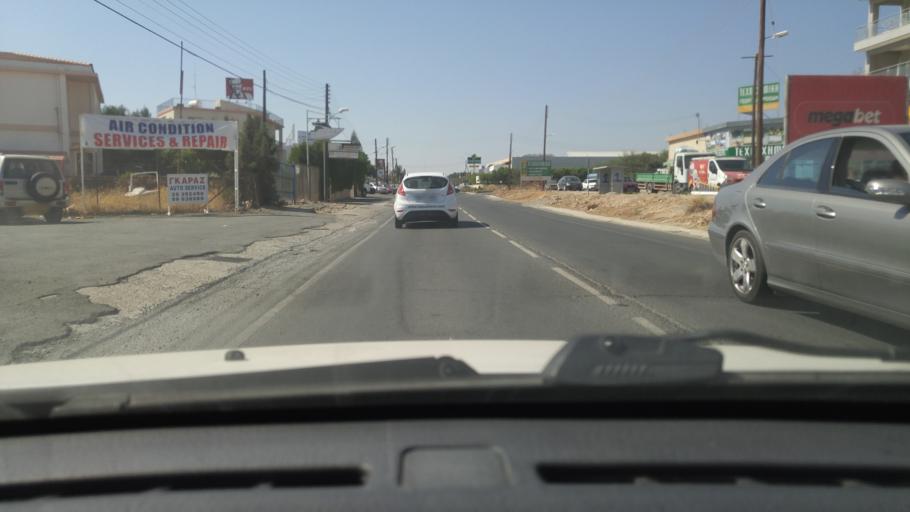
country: CY
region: Limassol
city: Ypsonas
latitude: 34.6818
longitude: 32.9748
